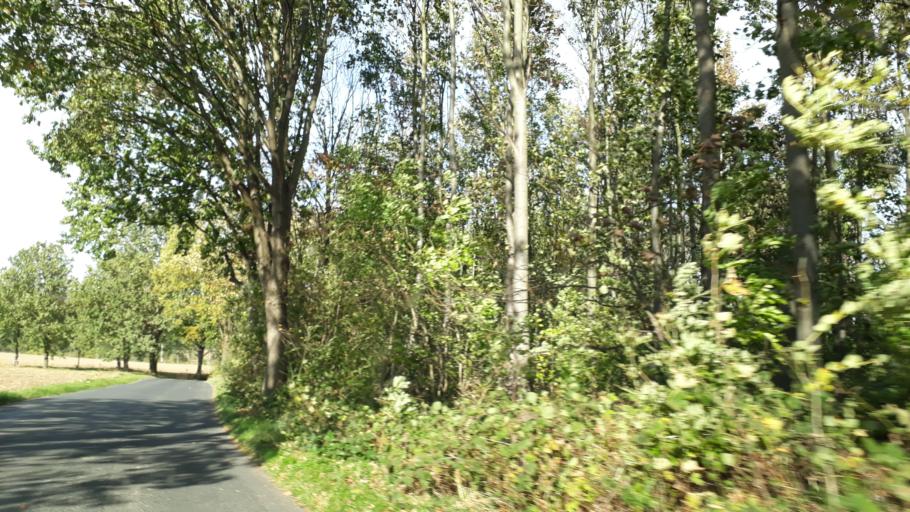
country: DE
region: Saxony
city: Ebersbach
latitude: 51.1080
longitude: 13.1386
